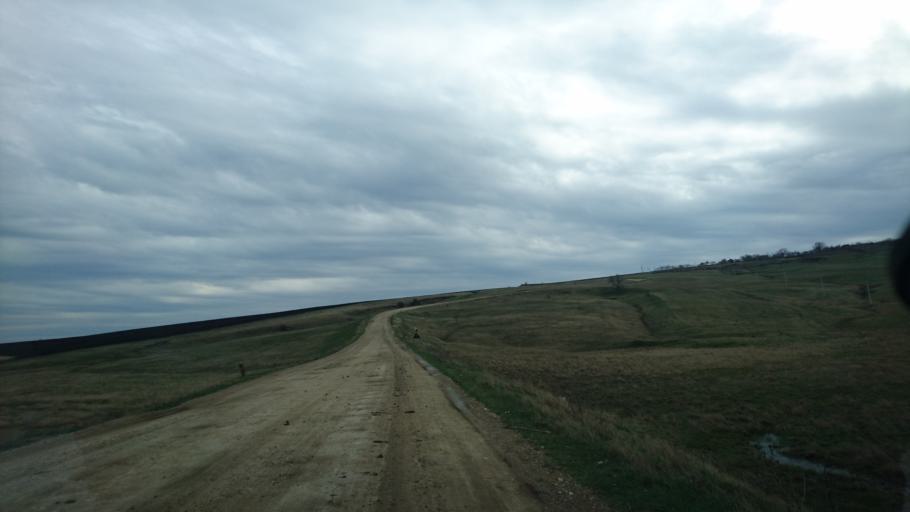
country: MD
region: Cantemir
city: Visniovca
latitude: 46.2921
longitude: 28.3953
